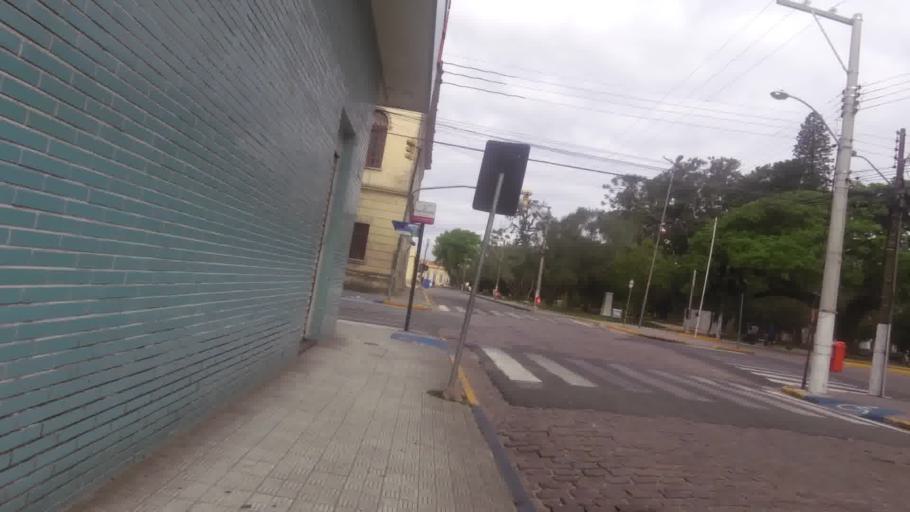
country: BR
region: Rio Grande do Sul
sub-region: Rio Grande
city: Rio Grande
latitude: -32.0301
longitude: -52.0978
